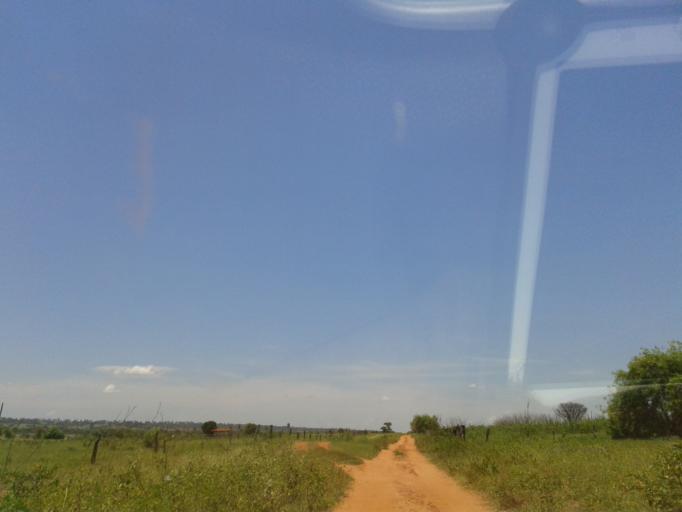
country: BR
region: Minas Gerais
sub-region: Santa Vitoria
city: Santa Vitoria
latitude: -19.2197
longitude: -50.4328
